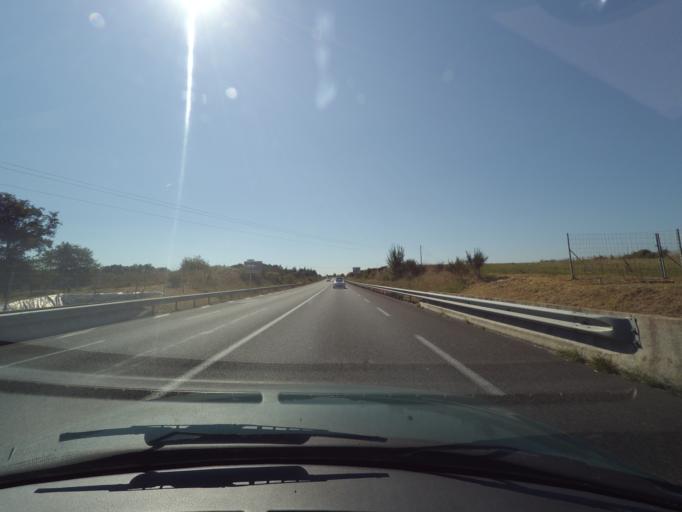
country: FR
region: Limousin
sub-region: Departement de la Haute-Vienne
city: Bellac
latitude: 46.1290
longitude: 1.0709
